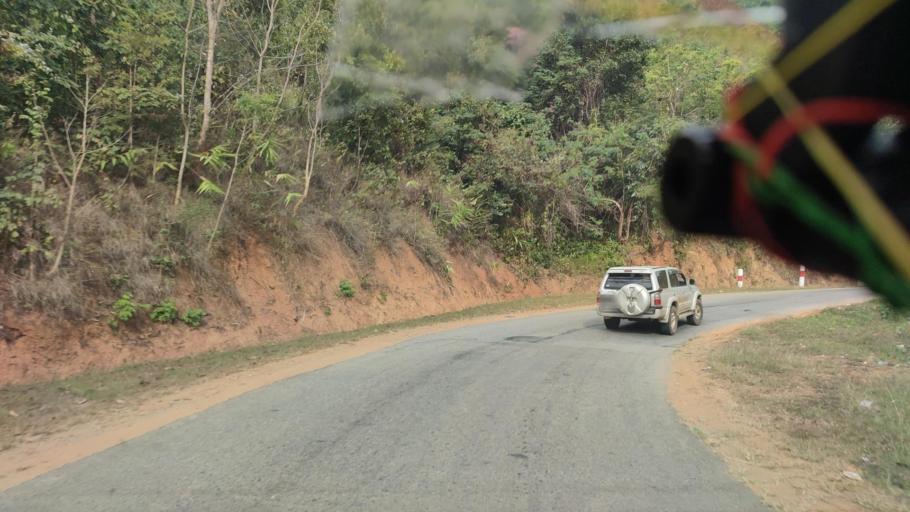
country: MM
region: Shan
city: Taunggyi
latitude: 21.2082
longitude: 97.6152
